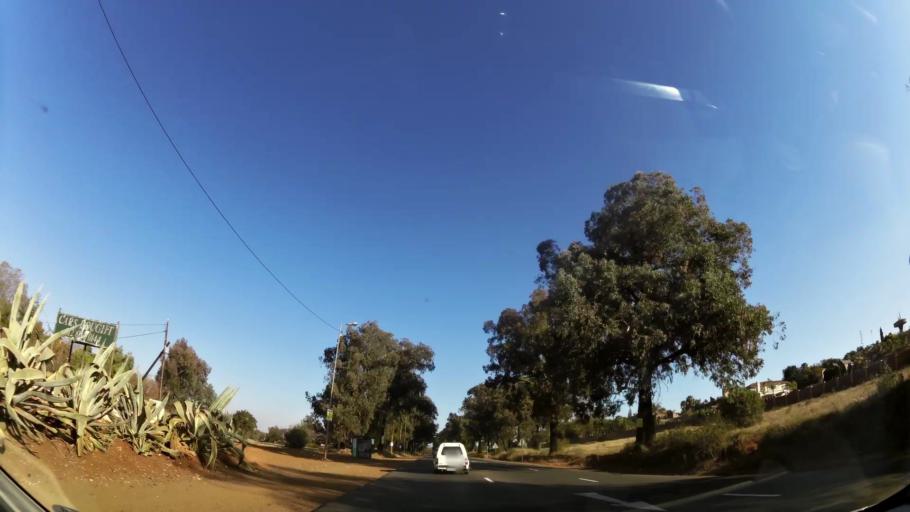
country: ZA
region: Gauteng
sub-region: City of Tshwane Metropolitan Municipality
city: Centurion
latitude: -25.8506
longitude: 28.1640
